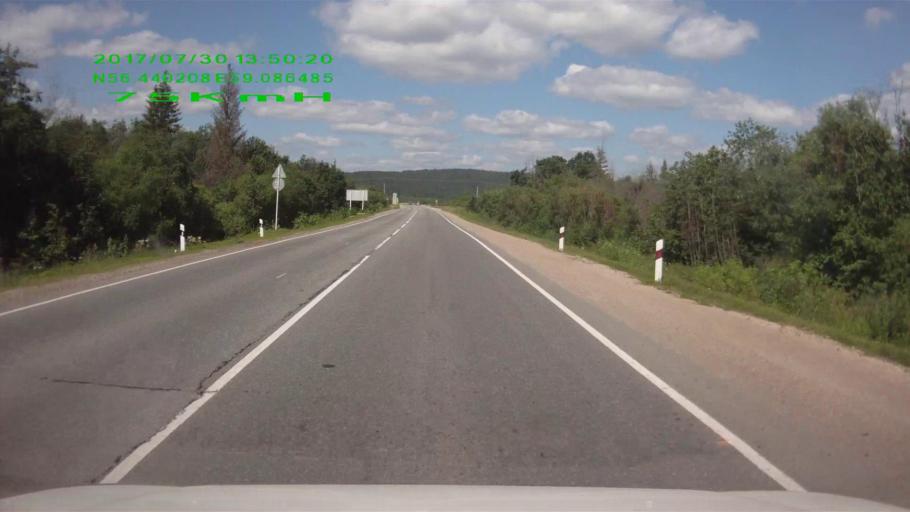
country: RU
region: Sverdlovsk
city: Mikhaylovsk
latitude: 56.4407
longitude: 59.0864
